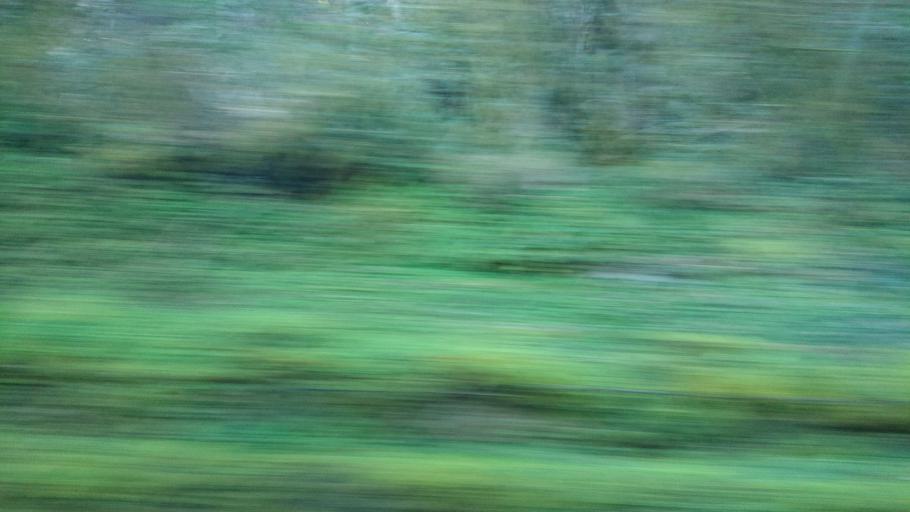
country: TW
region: Taiwan
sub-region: Hualien
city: Hualian
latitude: 24.4015
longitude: 121.3672
